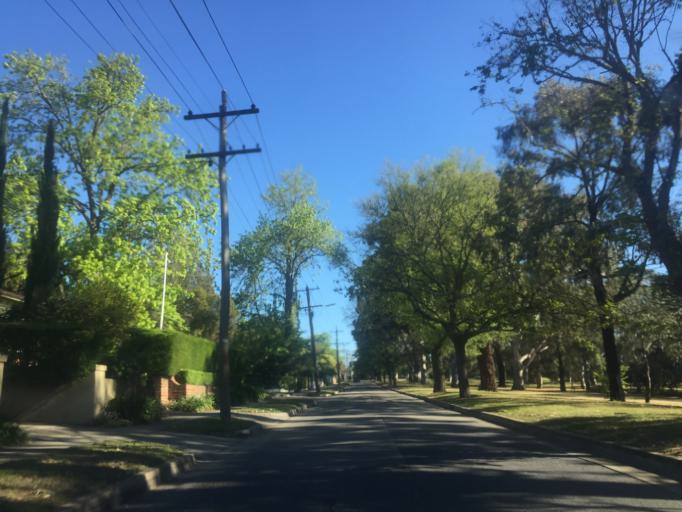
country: AU
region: Victoria
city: Balwyn
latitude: -37.8148
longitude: 145.0704
